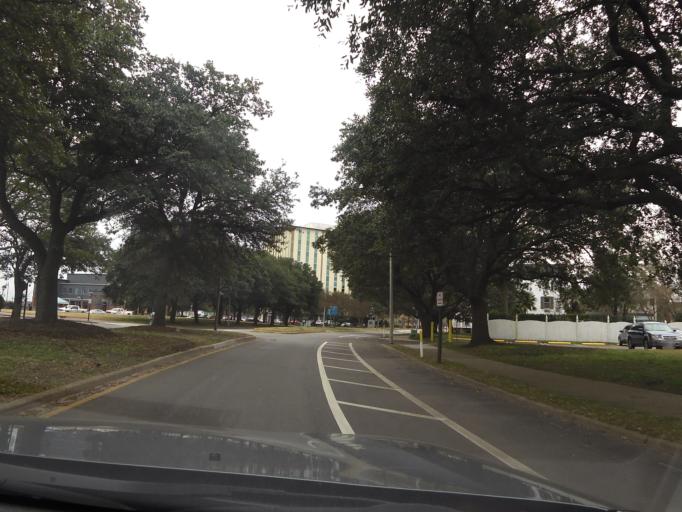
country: US
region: Virginia
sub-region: City of Portsmouth
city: Portsmouth
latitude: 36.8396
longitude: -76.2984
